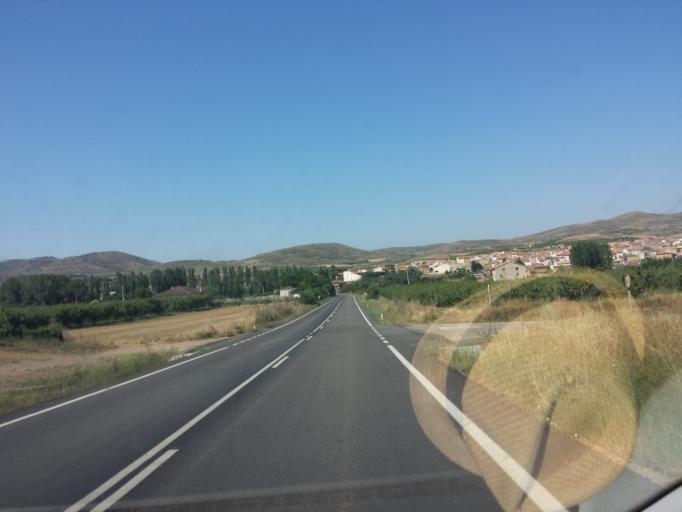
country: ES
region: Aragon
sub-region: Provincia de Zaragoza
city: Munebrega
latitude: 41.2525
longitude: -1.6976
